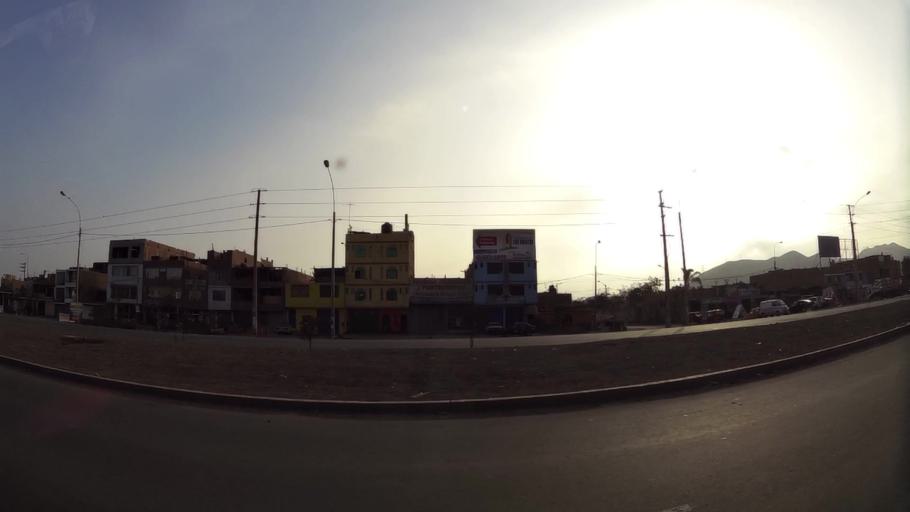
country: PE
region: Lima
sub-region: Lima
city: Independencia
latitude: -11.9512
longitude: -77.0853
